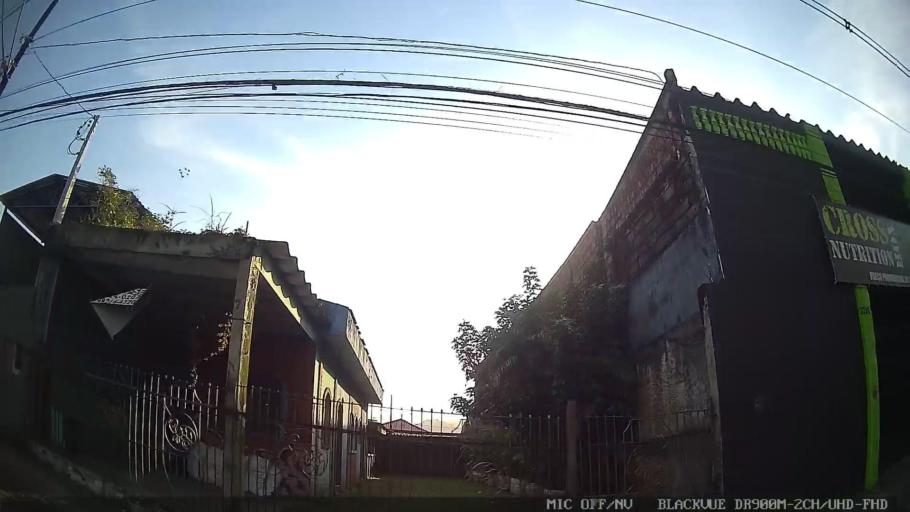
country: BR
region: Sao Paulo
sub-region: Cubatao
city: Cubatao
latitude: -23.8999
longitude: -46.4223
